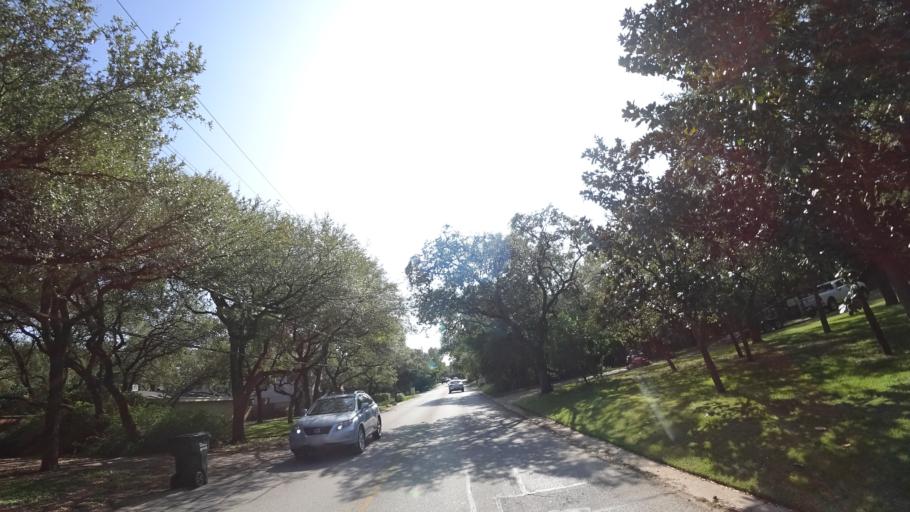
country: US
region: Texas
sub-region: Travis County
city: West Lake Hills
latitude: 30.2835
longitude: -97.8073
